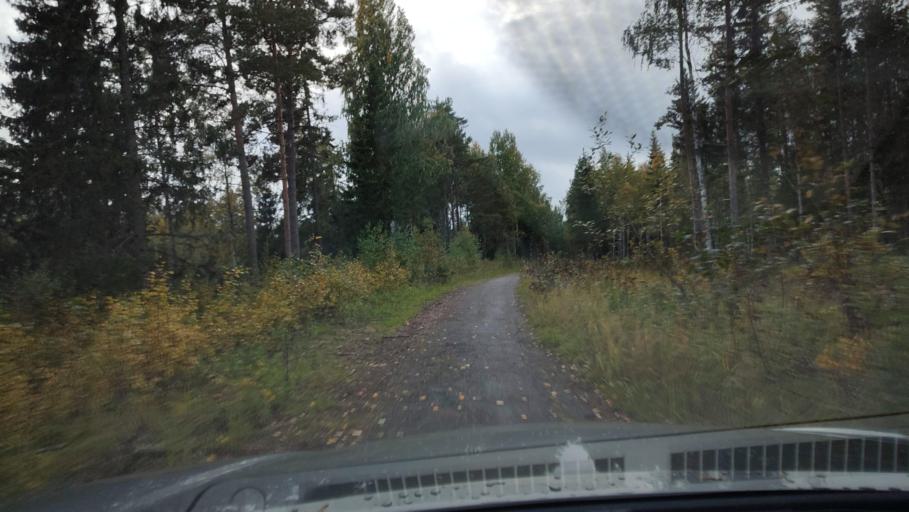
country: FI
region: Ostrobothnia
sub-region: Sydosterbotten
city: Kristinestad
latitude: 62.2675
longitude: 21.4173
